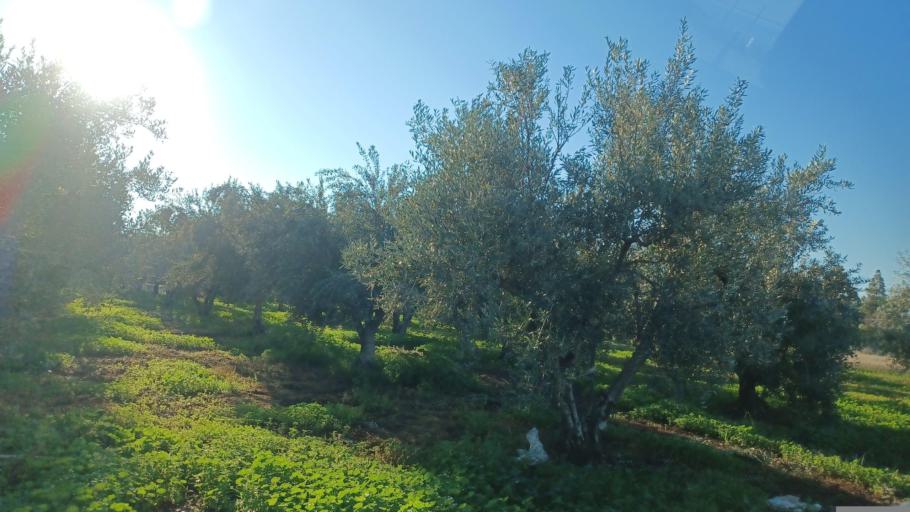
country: CY
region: Lefkosia
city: Astromeritis
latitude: 35.1466
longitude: 33.0366
